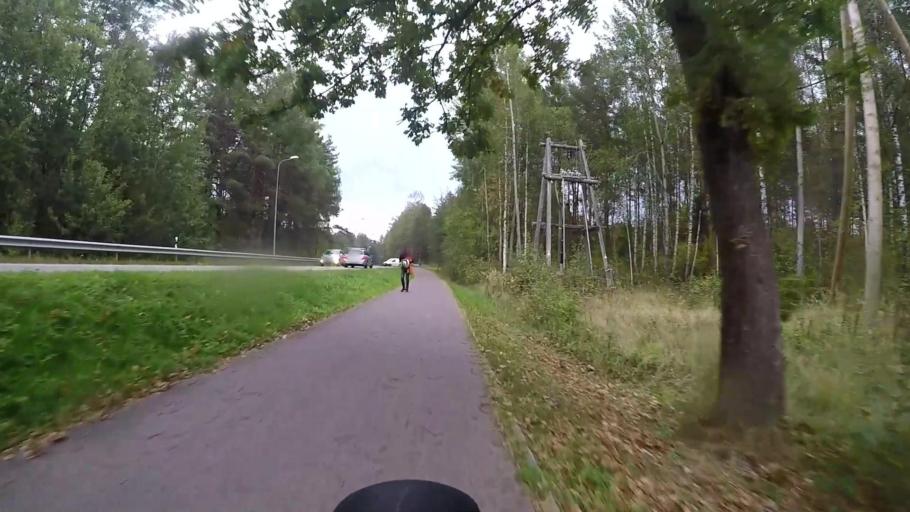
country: LV
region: Saulkrastu
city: Saulkrasti
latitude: 57.2659
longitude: 24.4270
